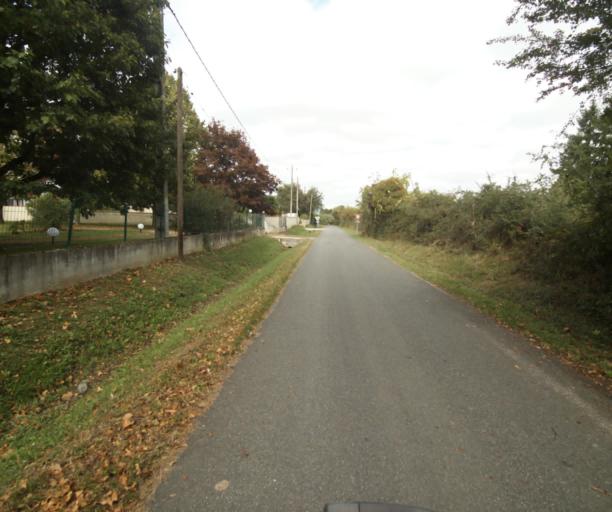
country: FR
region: Midi-Pyrenees
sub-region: Departement du Tarn-et-Garonne
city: Montech
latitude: 43.9563
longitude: 1.2234
